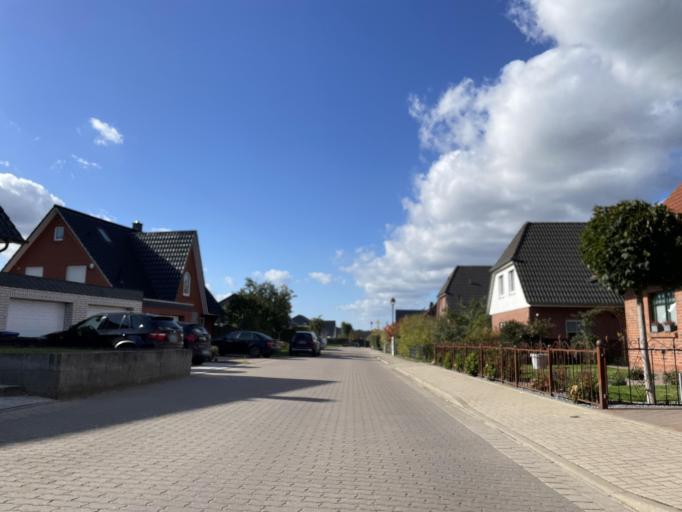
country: DE
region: Lower Saxony
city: Barendorf
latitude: 53.2342
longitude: 10.5233
